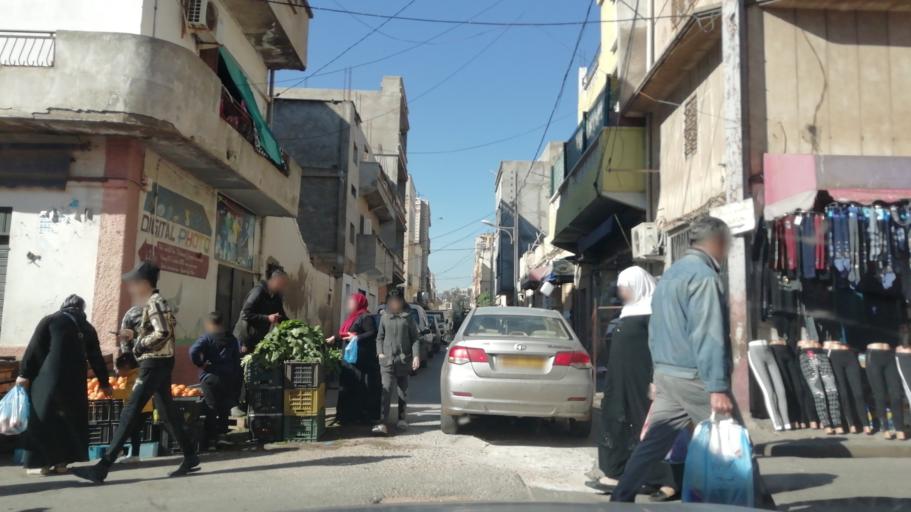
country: DZ
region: Oran
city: Oran
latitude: 35.6962
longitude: -0.6253
